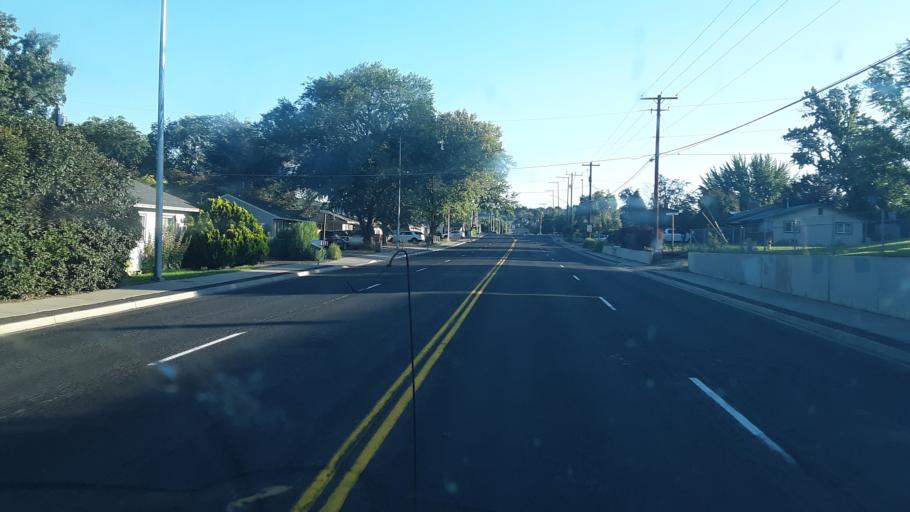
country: US
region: Washington
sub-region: Yakima County
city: West Valley
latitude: 46.5899
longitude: -120.6042
